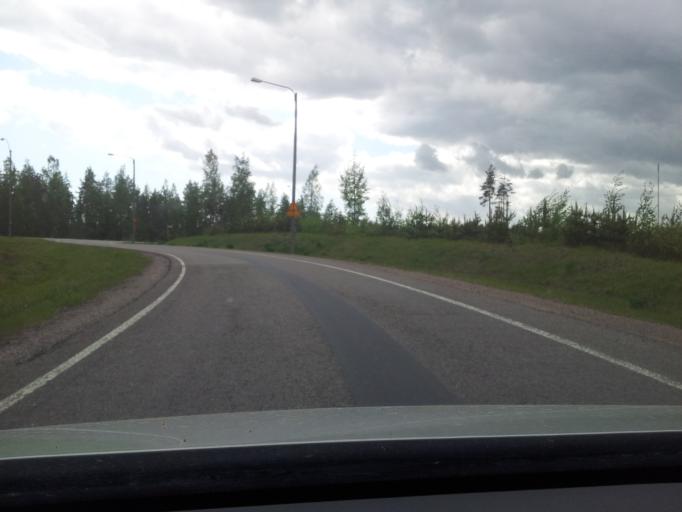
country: FI
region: South Karelia
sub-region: Lappeenranta
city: Luumaeki
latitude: 60.9291
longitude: 27.5814
